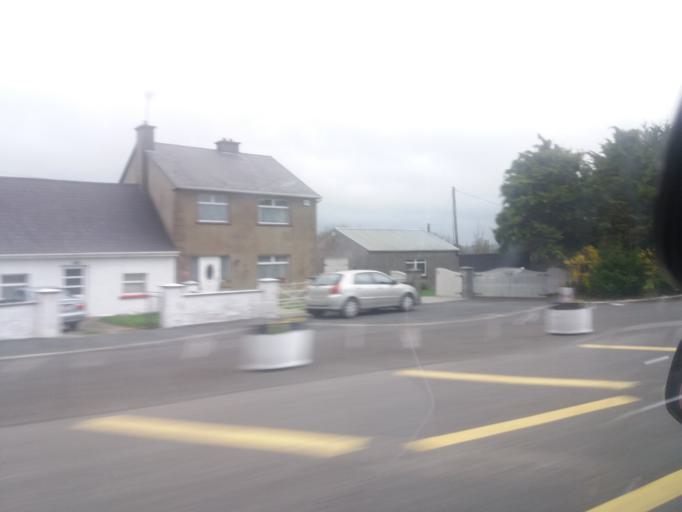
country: IE
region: Munster
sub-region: County Limerick
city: Rathkeale
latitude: 52.5029
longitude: -8.9918
